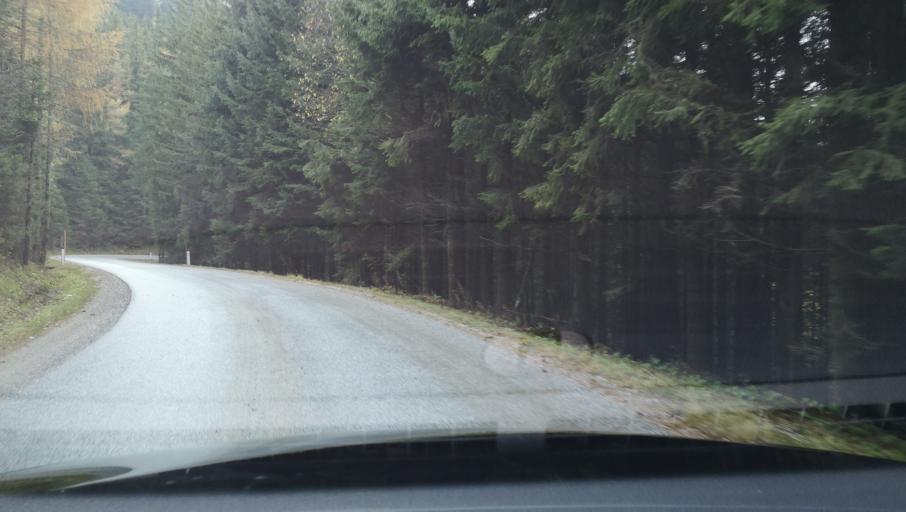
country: AT
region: Styria
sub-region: Politischer Bezirk Weiz
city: Gasen
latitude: 47.3583
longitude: 15.5884
